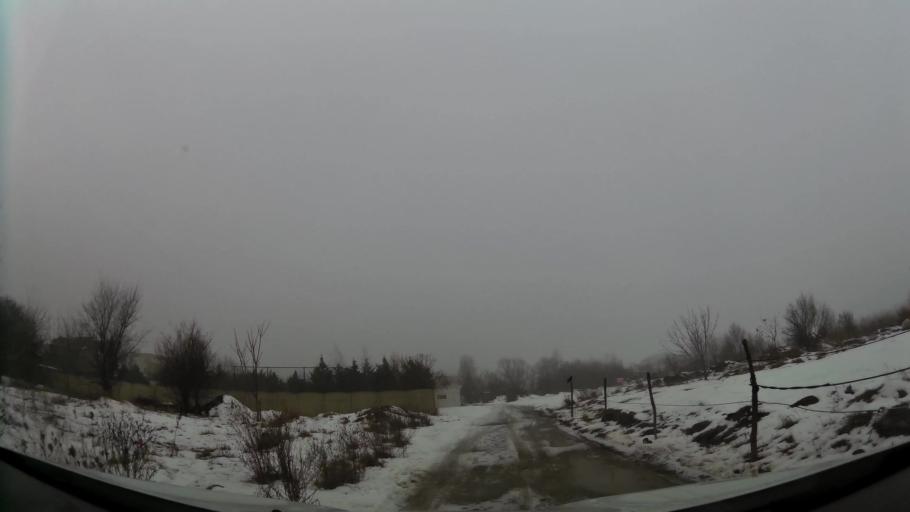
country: RO
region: Ilfov
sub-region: Comuna Chiajna
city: Rosu
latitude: 44.4474
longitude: 26.0273
